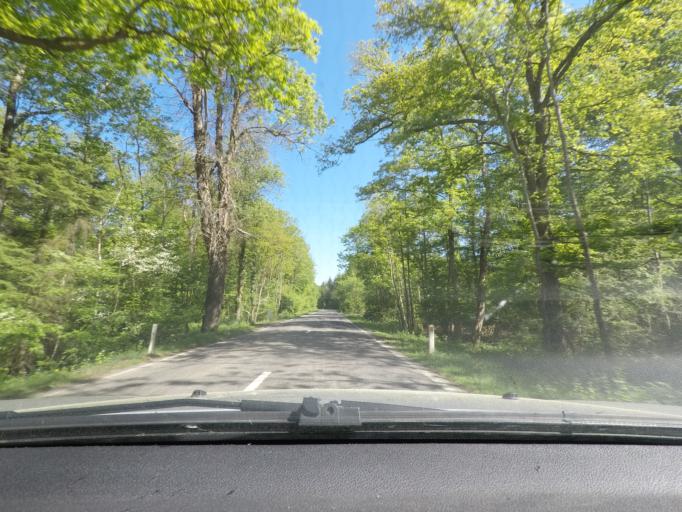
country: BE
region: Wallonia
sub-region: Province du Luxembourg
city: Wellin
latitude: 50.1794
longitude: 5.1199
